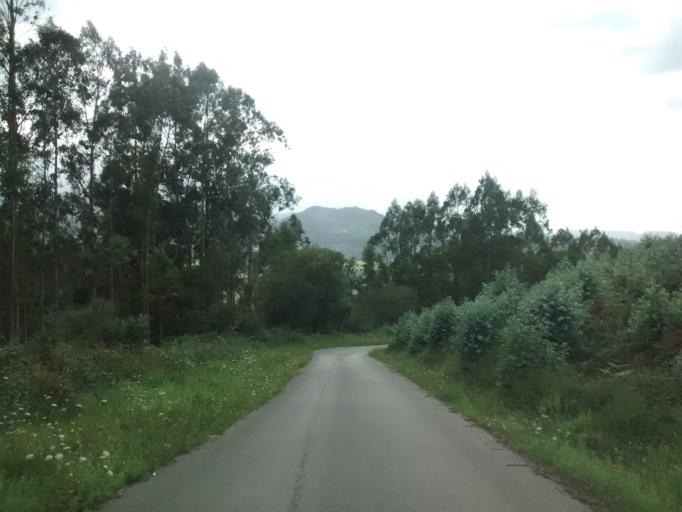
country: ES
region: Cantabria
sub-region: Provincia de Cantabria
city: Comillas
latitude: 43.3393
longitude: -4.3183
